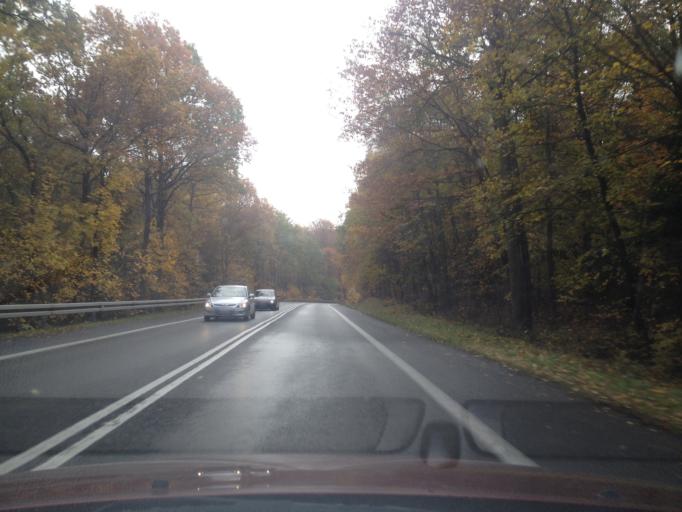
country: PL
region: Lower Silesian Voivodeship
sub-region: Powiat lubanski
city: Siekierczyn
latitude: 51.1616
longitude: 15.1455
